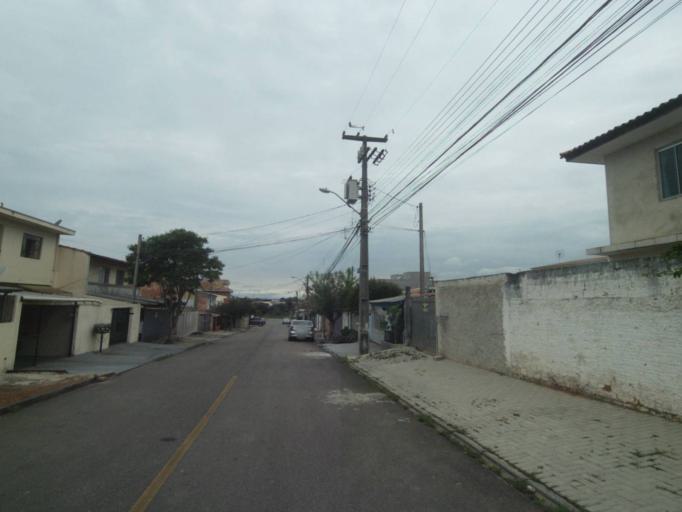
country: BR
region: Parana
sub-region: Sao Jose Dos Pinhais
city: Sao Jose dos Pinhais
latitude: -25.5514
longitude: -49.2606
